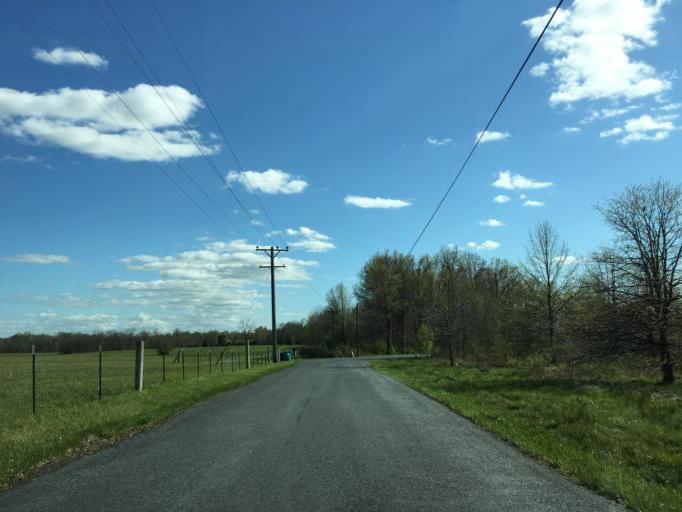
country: US
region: Maryland
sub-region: Frederick County
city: Thurmont
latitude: 39.6481
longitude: -77.3862
